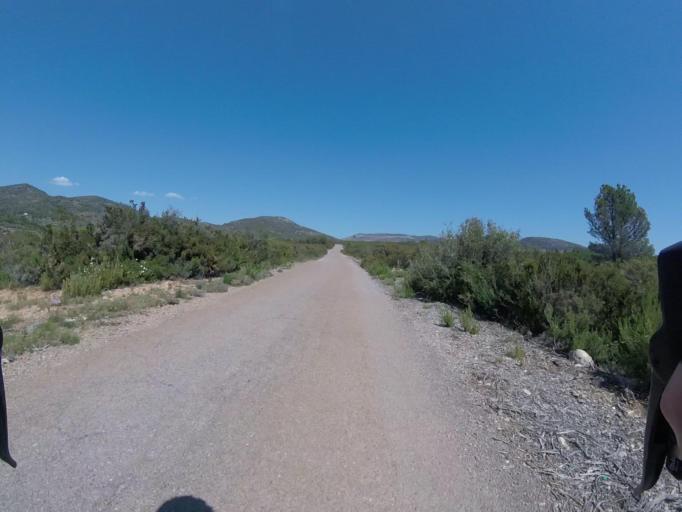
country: ES
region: Valencia
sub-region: Provincia de Castello
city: Sierra-Engarceran
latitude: 40.2408
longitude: -0.0263
